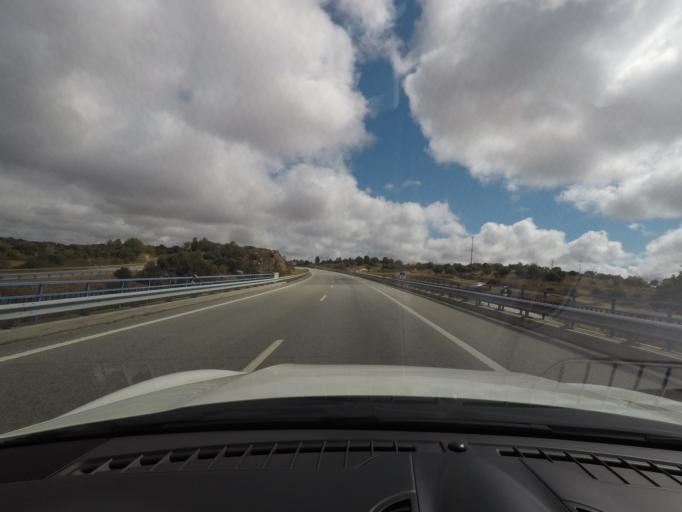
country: ES
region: Castille and Leon
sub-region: Provincia de Salamanca
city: Fuentes de Onoro
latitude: 40.6127
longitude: -6.8886
